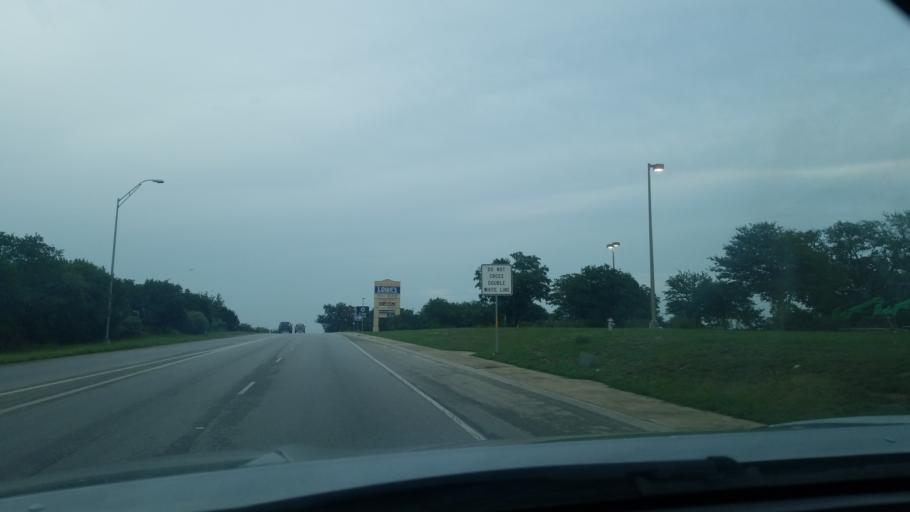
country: US
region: Texas
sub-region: Bexar County
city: Hollywood Park
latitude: 29.6081
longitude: -98.5145
